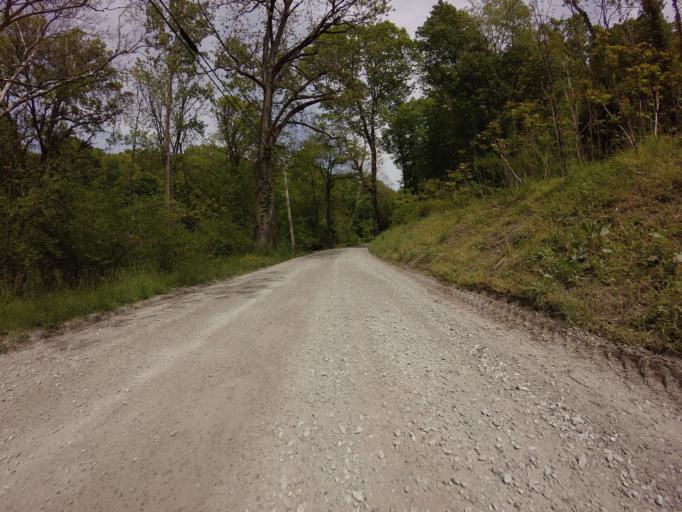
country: US
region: Maryland
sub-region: Carroll County
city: New Windsor
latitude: 39.4993
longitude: -77.1116
